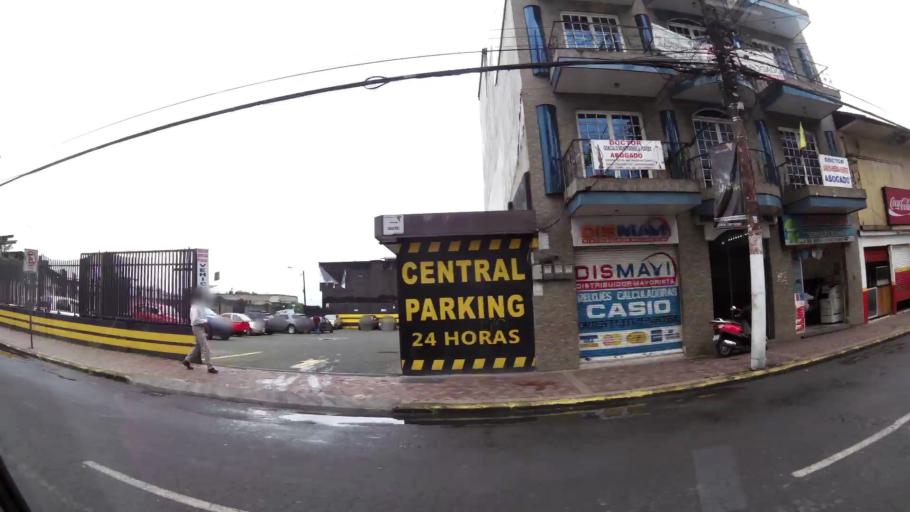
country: EC
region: Santo Domingo de los Tsachilas
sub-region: Canton Santo Domingo de los Colorados
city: Santo Domingo de los Colorados
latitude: -0.2543
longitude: -79.1673
